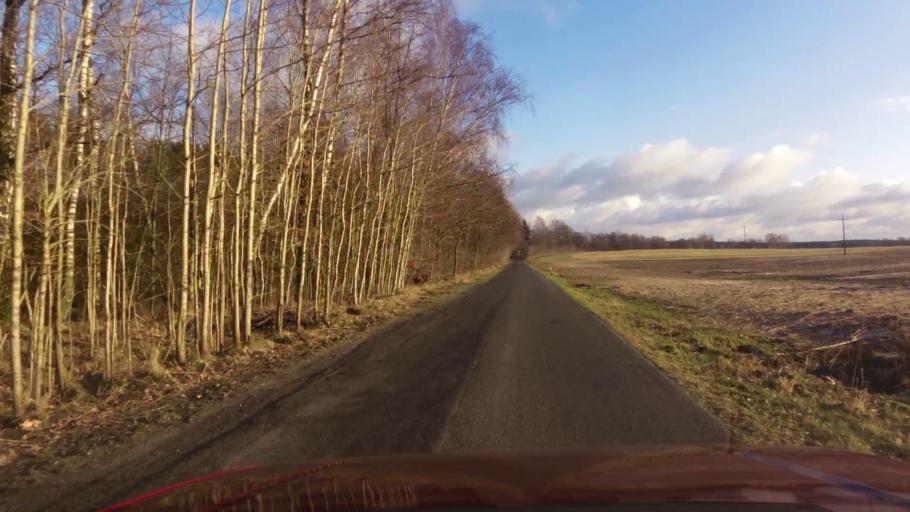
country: PL
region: West Pomeranian Voivodeship
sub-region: Koszalin
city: Koszalin
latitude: 54.0701
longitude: 16.1525
